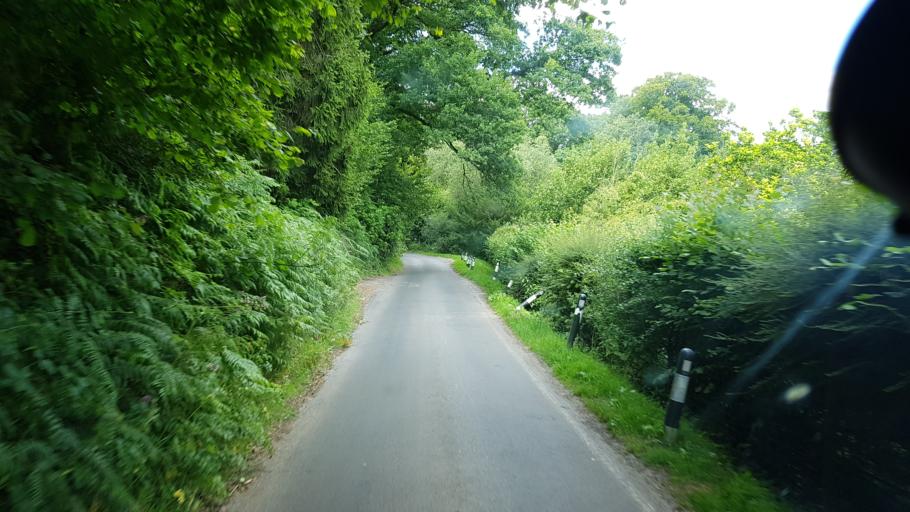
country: GB
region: England
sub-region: West Sussex
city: South Nutfield
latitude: 51.0590
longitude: -0.1213
